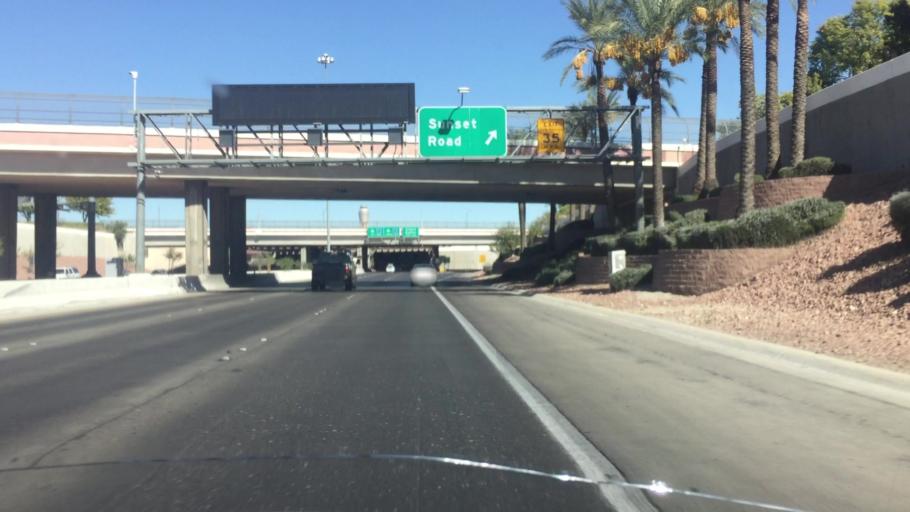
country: US
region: Nevada
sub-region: Clark County
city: Paradise
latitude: 36.0695
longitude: -115.1468
